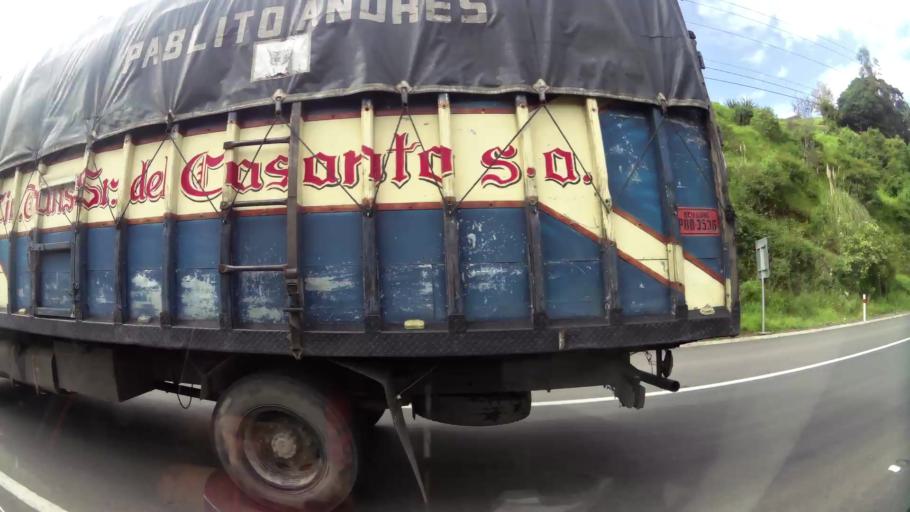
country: EC
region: Pichincha
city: Sangolqui
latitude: -0.3222
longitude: -78.4038
